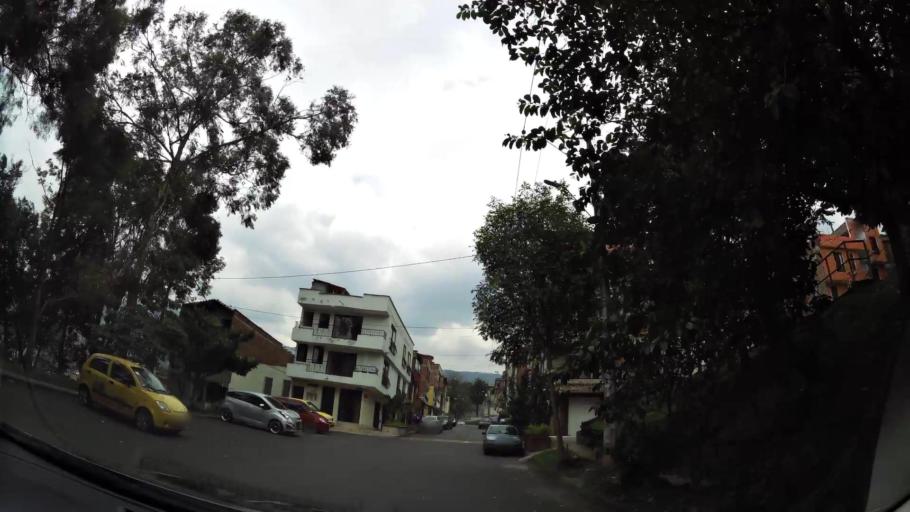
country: CO
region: Antioquia
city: Medellin
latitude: 6.2334
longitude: -75.5499
